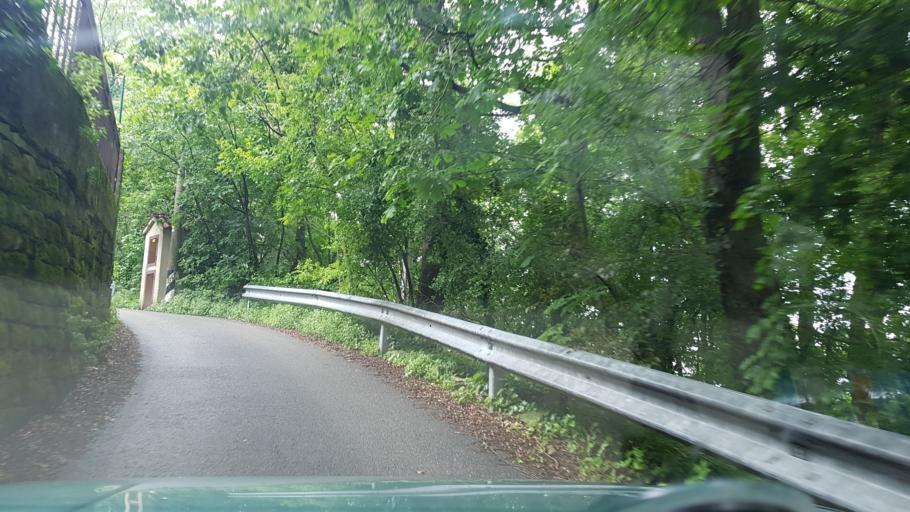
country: IT
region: Friuli Venezia Giulia
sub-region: Provincia di Trieste
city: Villa Opicina
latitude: 45.6734
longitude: 13.7813
